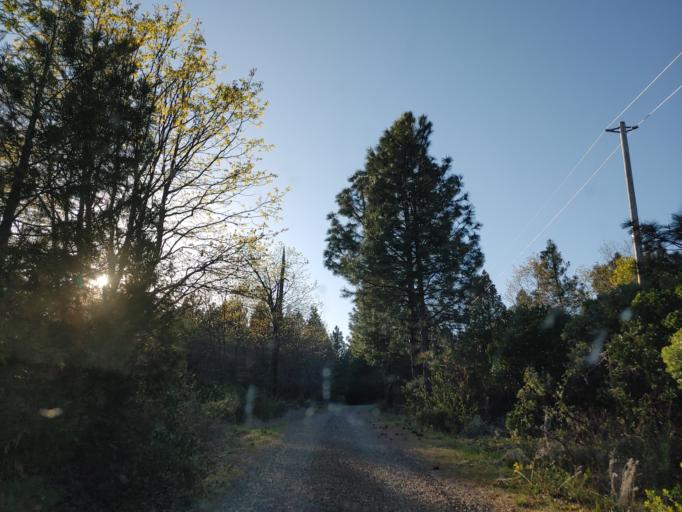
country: US
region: California
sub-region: Shasta County
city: Burney
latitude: 40.8113
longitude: -121.9451
